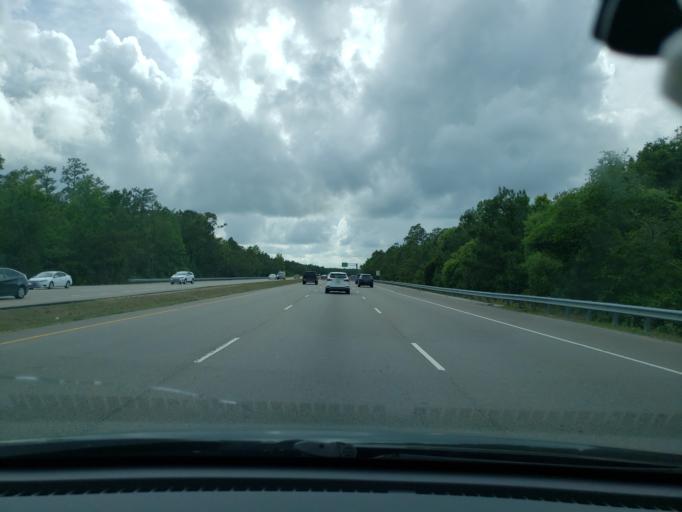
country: US
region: North Carolina
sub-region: New Hanover County
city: Kings Grant
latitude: 34.2541
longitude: -77.8908
